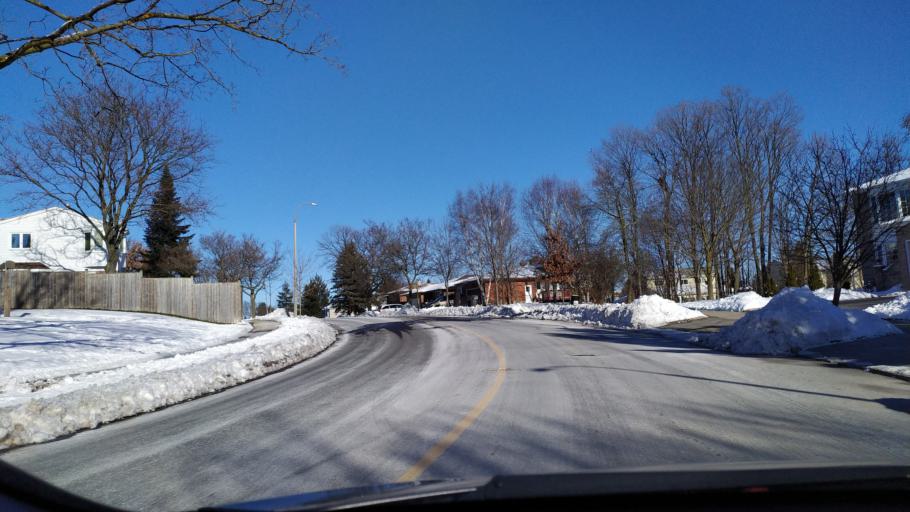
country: CA
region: Ontario
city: Waterloo
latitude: 43.4481
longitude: -80.5588
